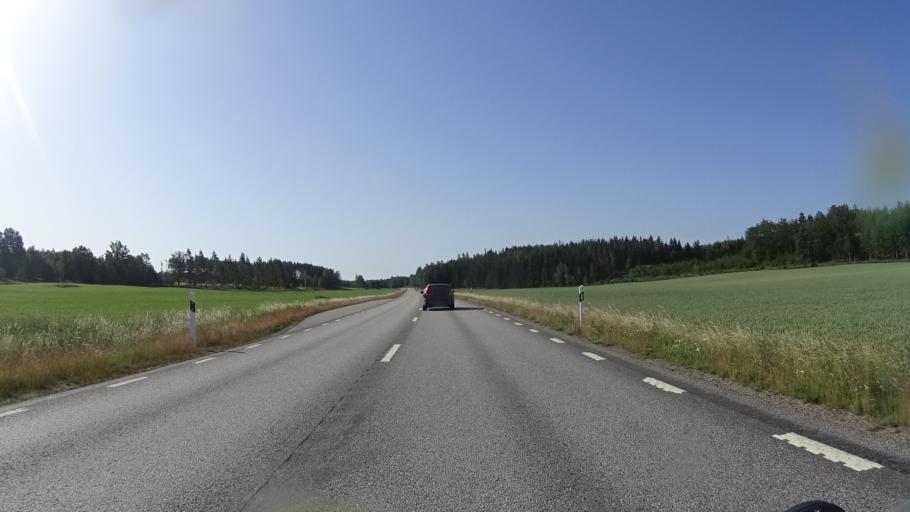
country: SE
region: OEstergoetland
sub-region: Linkopings Kommun
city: Sturefors
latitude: 58.3359
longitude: 15.8497
